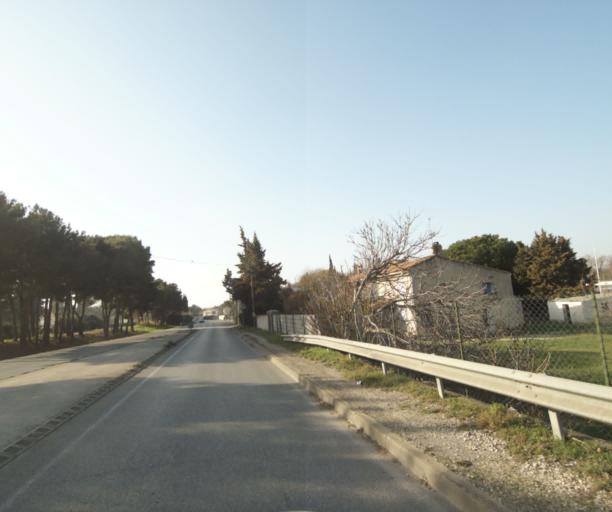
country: FR
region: Provence-Alpes-Cote d'Azur
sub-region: Departement des Bouches-du-Rhone
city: Les Pennes-Mirabeau
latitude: 43.4160
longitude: 5.2951
